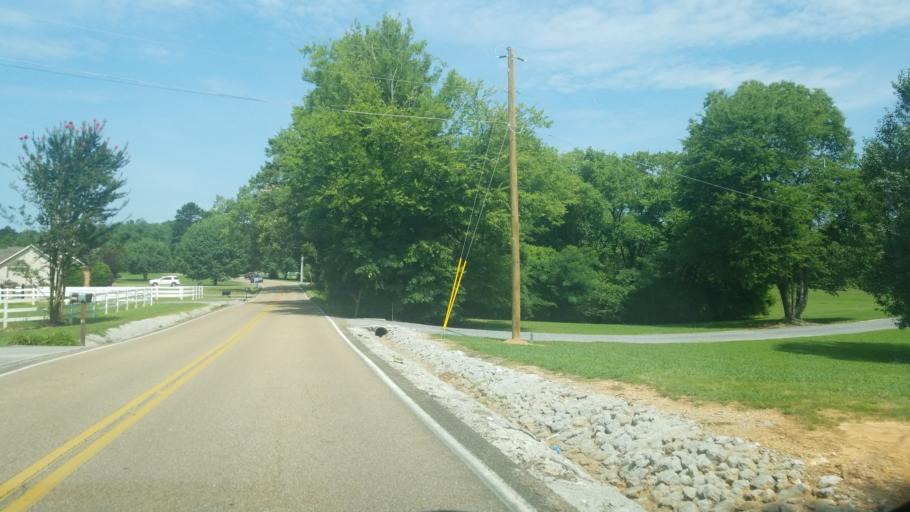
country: US
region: Tennessee
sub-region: Hamilton County
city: Lakesite
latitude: 35.1676
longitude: -85.0607
